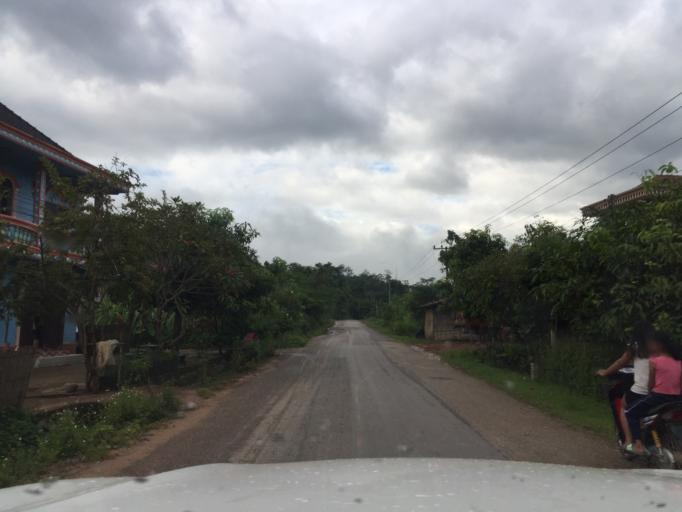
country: LA
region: Oudomxai
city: Muang La
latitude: 20.8530
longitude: 102.1093
